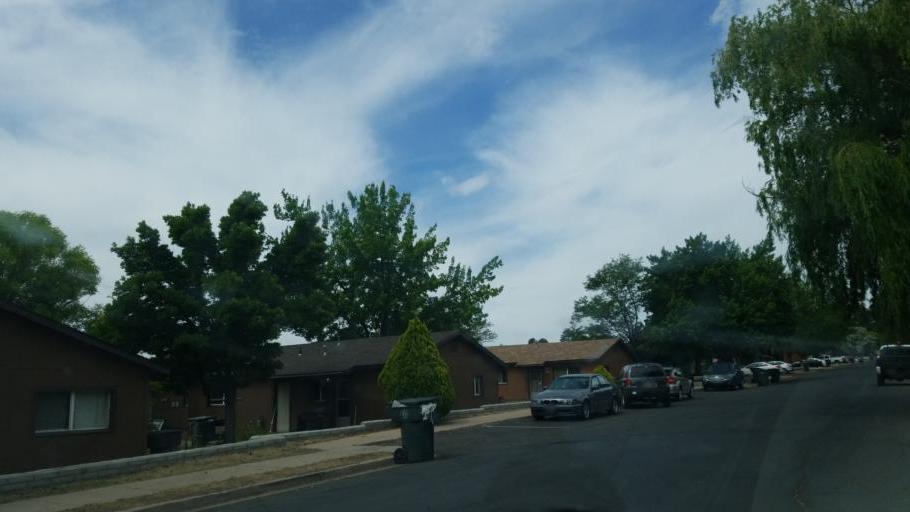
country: US
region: Arizona
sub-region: Coconino County
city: Flagstaff
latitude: 35.2166
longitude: -111.5961
